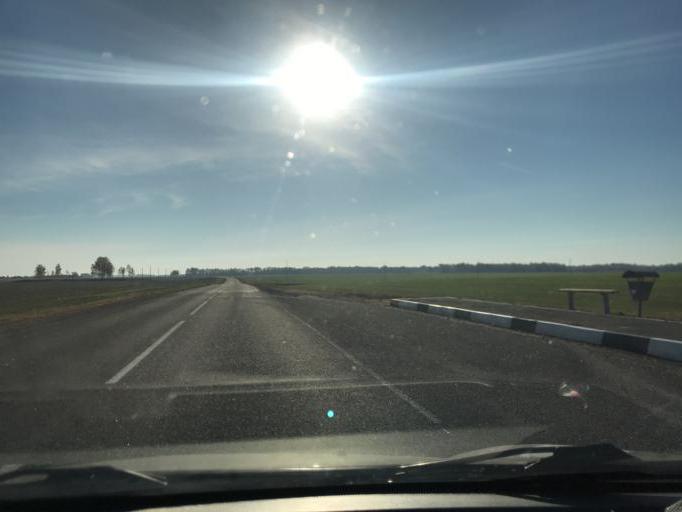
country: BY
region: Gomel
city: Brahin
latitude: 51.8055
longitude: 30.1161
